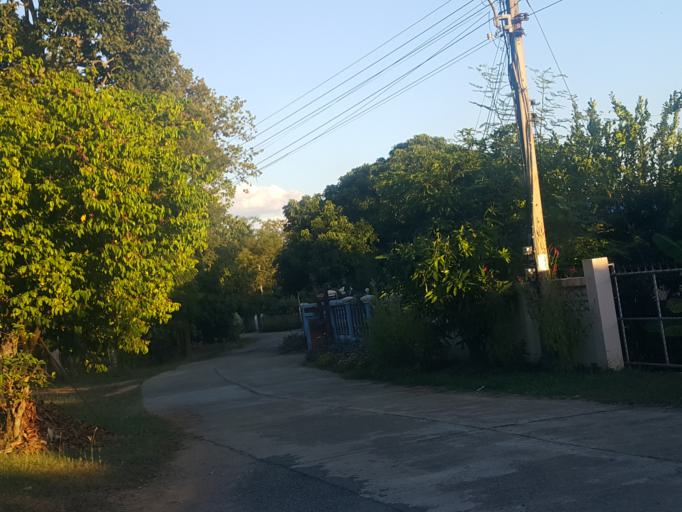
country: TH
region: Chiang Mai
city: San Sai
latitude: 18.8626
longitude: 99.1485
